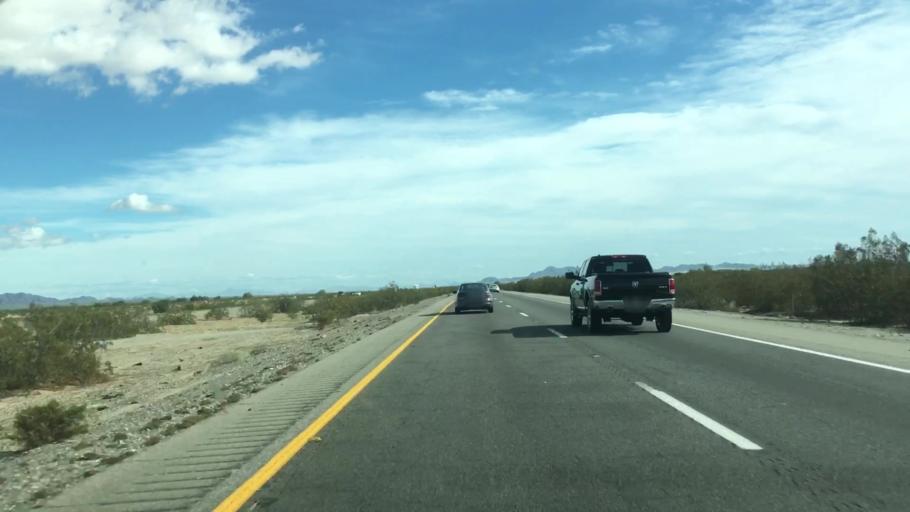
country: US
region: California
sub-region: Riverside County
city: Mesa Verde
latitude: 33.6198
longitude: -115.0323
